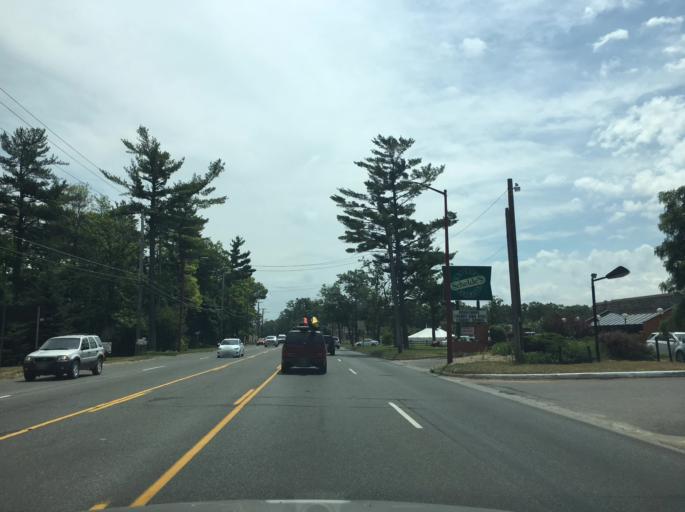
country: US
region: Michigan
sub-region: Grand Traverse County
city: Traverse City
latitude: 44.7561
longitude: -85.5749
